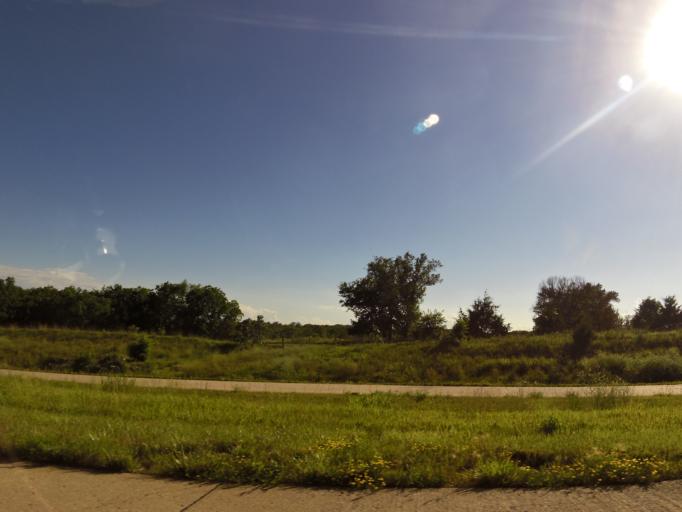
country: US
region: Missouri
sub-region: Ralls County
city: New London
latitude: 39.5019
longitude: -91.3197
